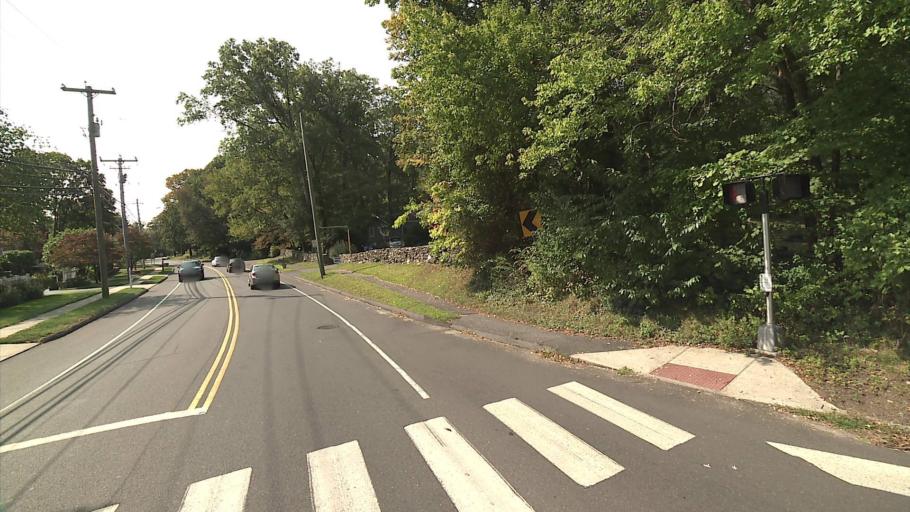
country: US
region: Connecticut
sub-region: Fairfield County
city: Fairfield
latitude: 41.1748
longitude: -73.2583
